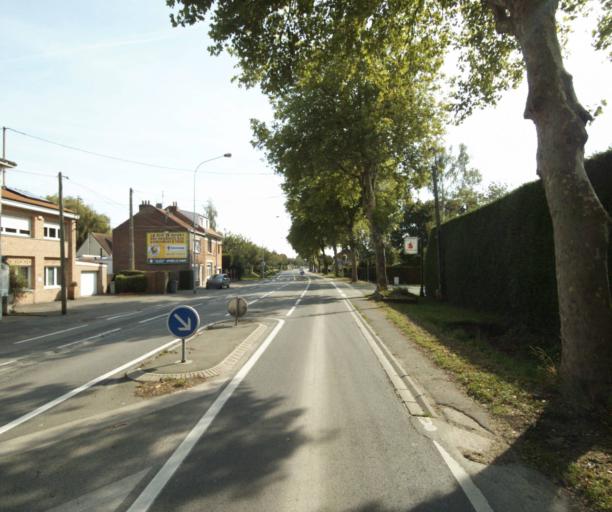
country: FR
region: Nord-Pas-de-Calais
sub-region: Departement du Nord
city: Capinghem
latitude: 50.6478
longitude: 2.9547
